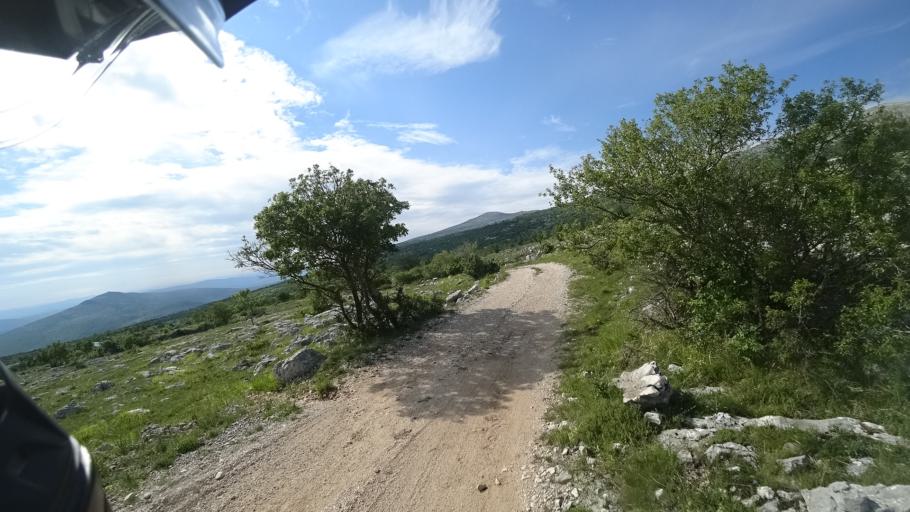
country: HR
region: Splitsko-Dalmatinska
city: Hrvace
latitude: 43.7796
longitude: 16.4504
